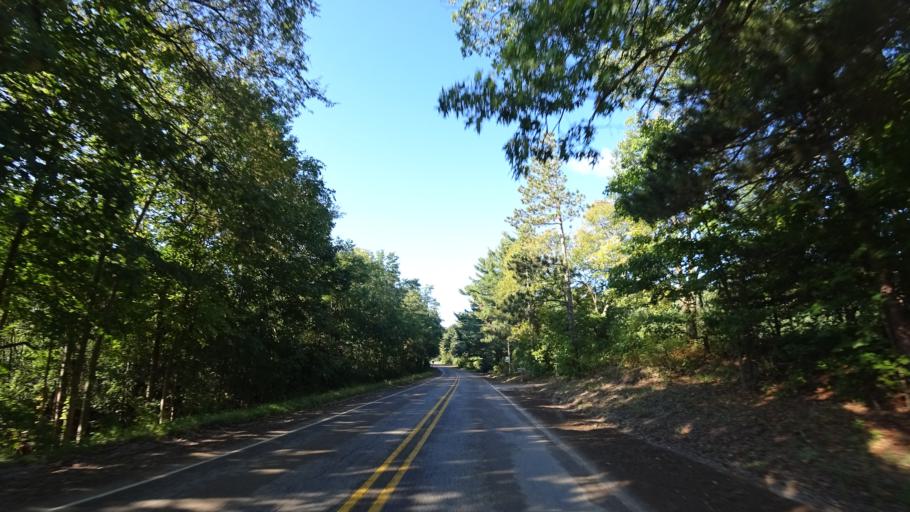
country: US
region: Michigan
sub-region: Kent County
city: Grandville
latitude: 42.9467
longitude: -85.7497
